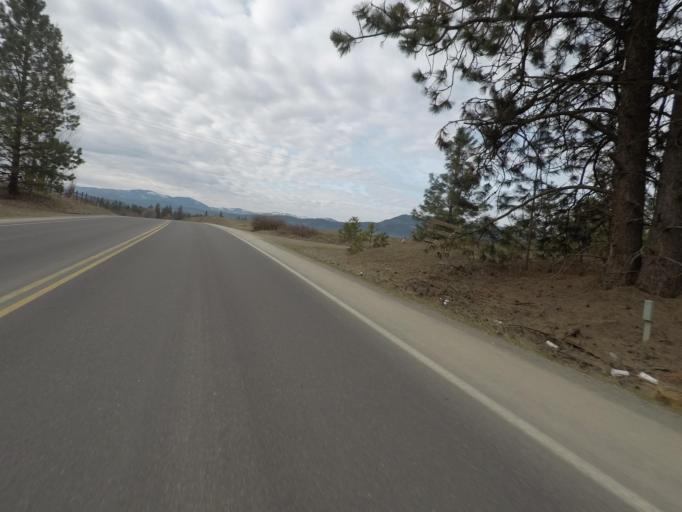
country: US
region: Washington
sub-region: Stevens County
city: Colville
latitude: 48.5565
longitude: -117.8815
